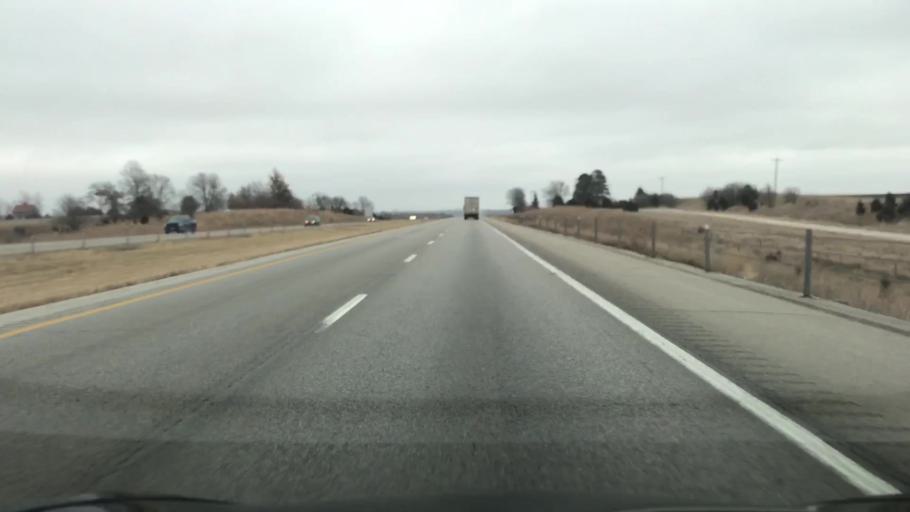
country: US
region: Iowa
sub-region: Madison County
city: Earlham
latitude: 41.5178
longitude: -94.1798
